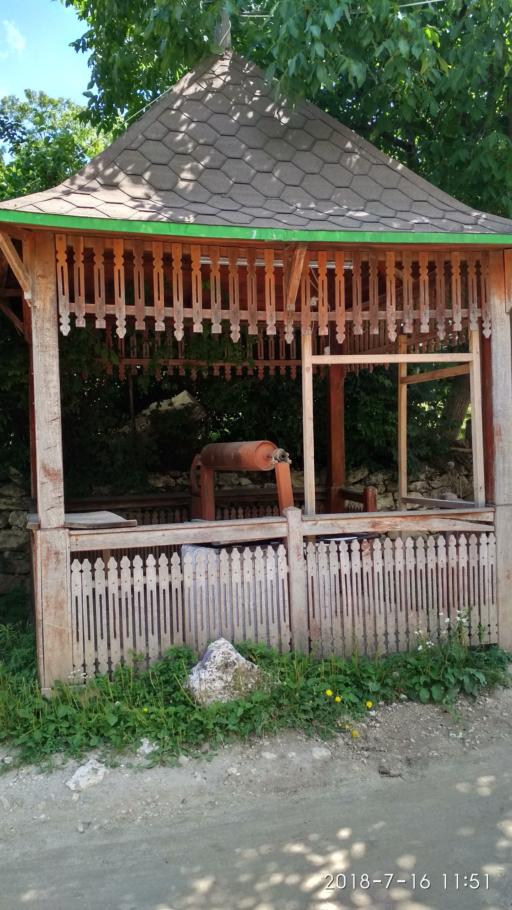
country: MD
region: Telenesti
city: Cocieri
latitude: 47.3061
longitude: 28.9609
